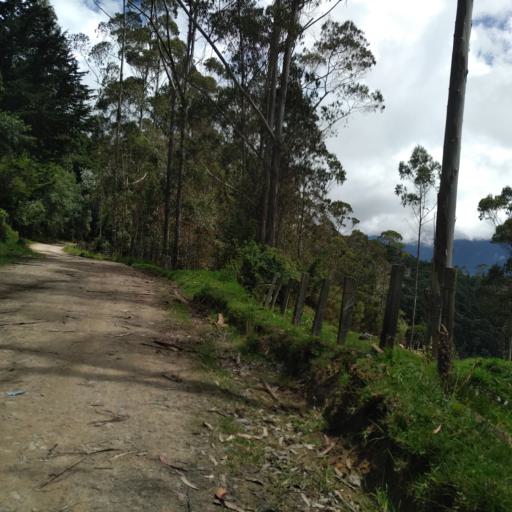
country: CO
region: Boyaca
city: Duitama
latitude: 5.9454
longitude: -73.1409
